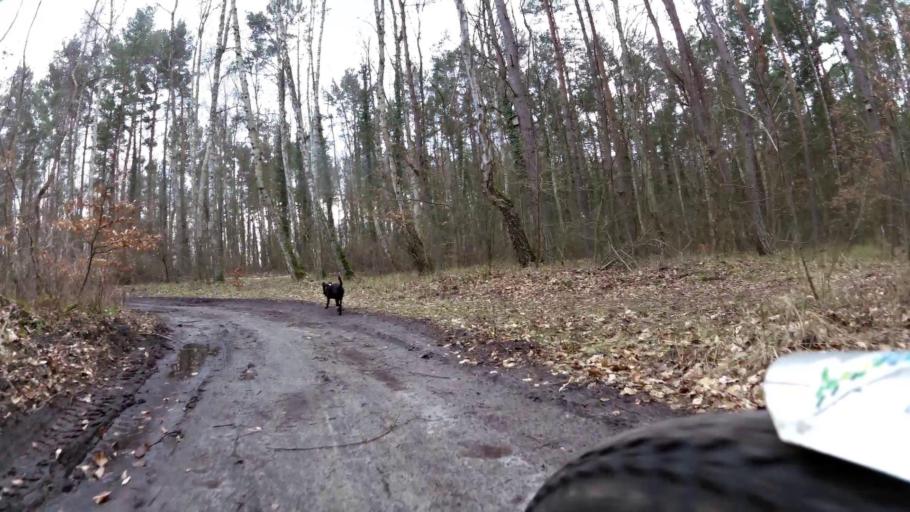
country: PL
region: West Pomeranian Voivodeship
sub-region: Powiat kamienski
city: Dziwnow
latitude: 54.0316
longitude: 14.7797
